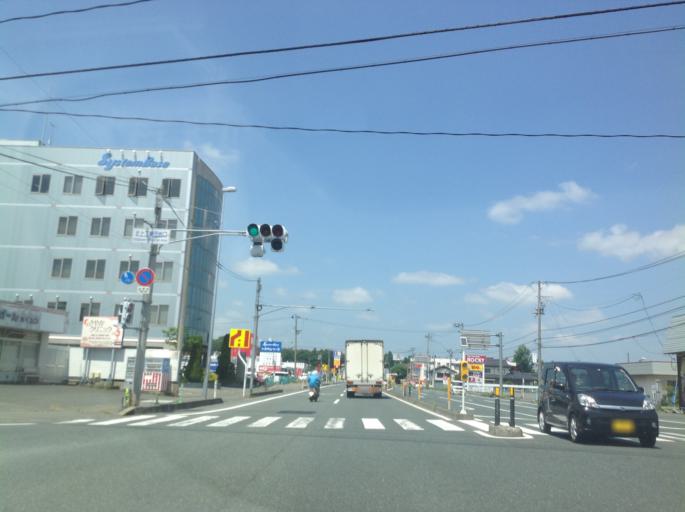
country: JP
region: Iwate
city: Hanamaki
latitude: 39.3360
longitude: 141.1089
